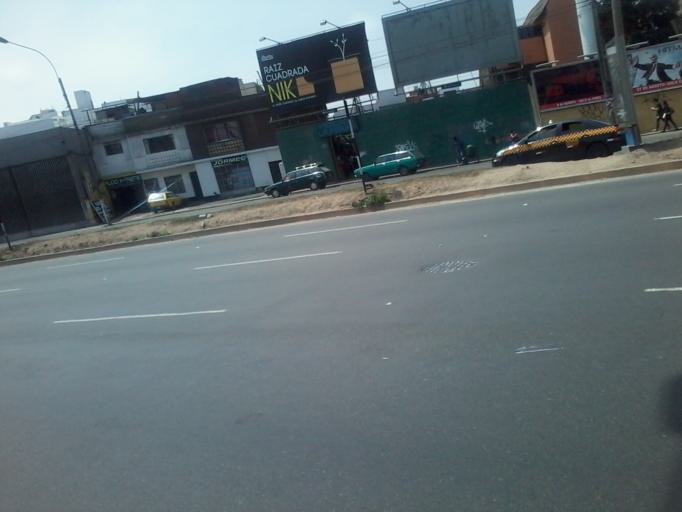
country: PE
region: Lima
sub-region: Lima
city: San Isidro
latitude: -12.0846
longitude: -77.0648
